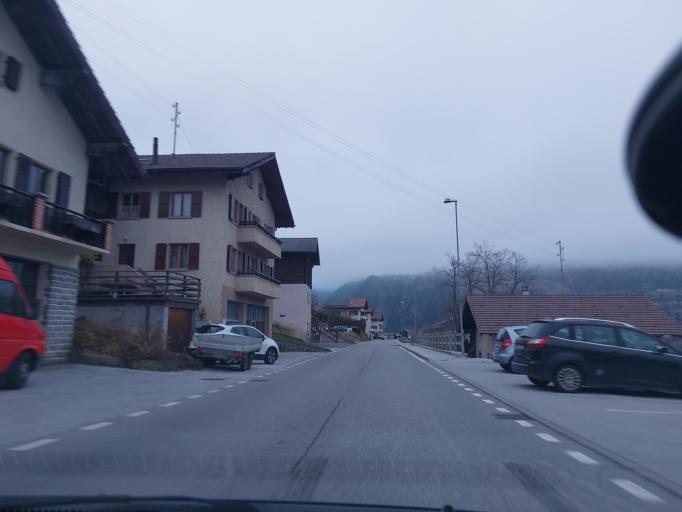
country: CH
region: Valais
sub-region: Herens District
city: Ayent
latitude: 46.2844
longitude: 7.4202
